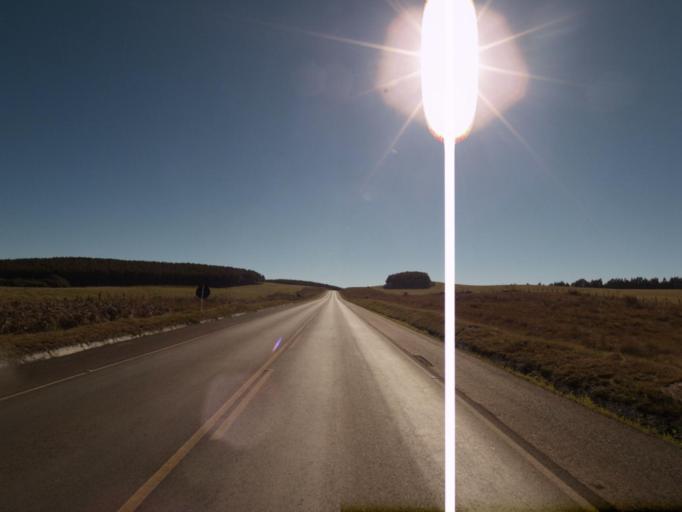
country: BR
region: Parana
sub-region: Palmas
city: Palmas
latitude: -26.7535
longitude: -51.6635
